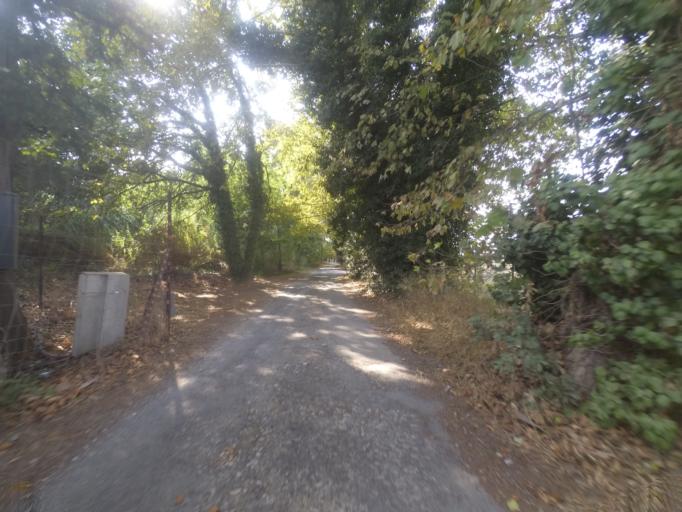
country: FR
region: Languedoc-Roussillon
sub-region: Departement des Pyrenees-Orientales
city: Le Soler
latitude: 42.6861
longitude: 2.7833
